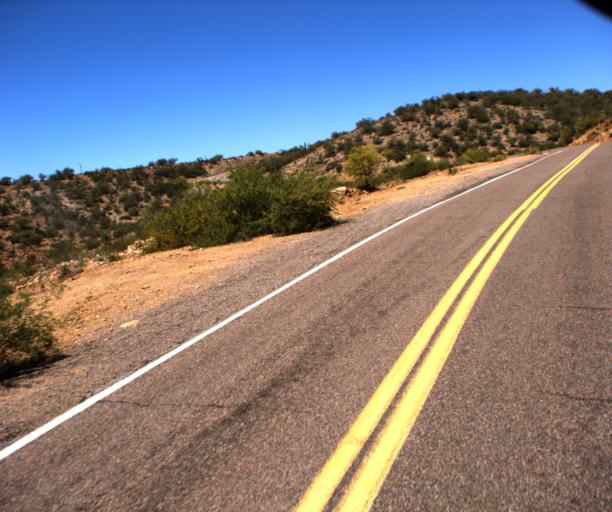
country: US
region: Arizona
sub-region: Yavapai County
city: Bagdad
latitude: 34.4554
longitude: -112.9962
